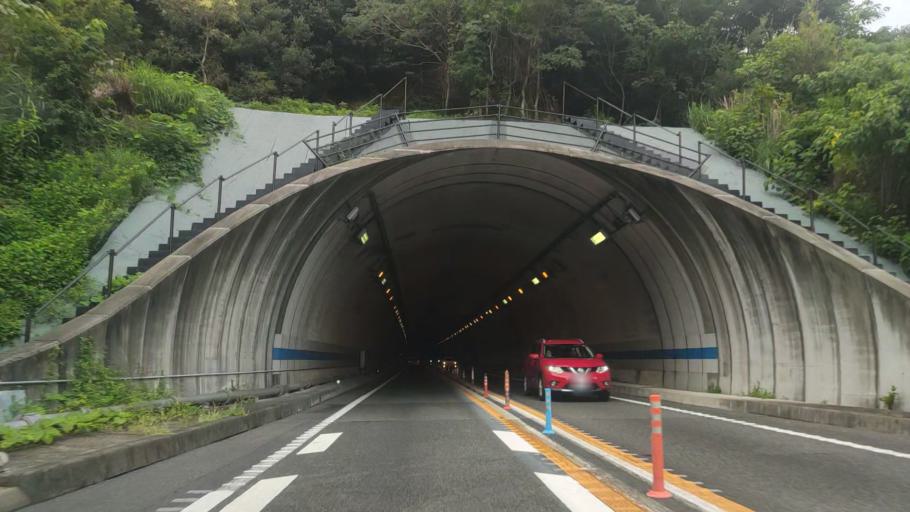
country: JP
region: Wakayama
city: Tanabe
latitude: 33.8034
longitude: 135.2685
